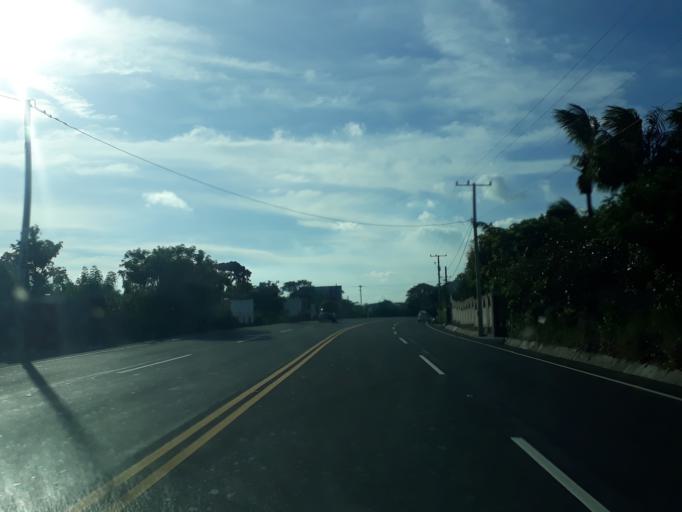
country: NI
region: Carazo
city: Diriamba
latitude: 11.9065
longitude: -86.2613
